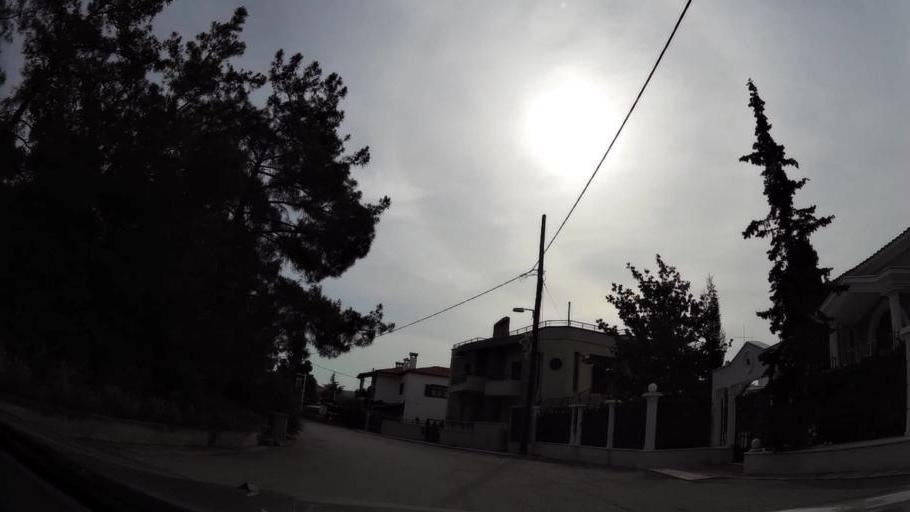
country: GR
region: Central Macedonia
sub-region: Nomos Thessalonikis
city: Panorama
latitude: 40.5864
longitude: 23.0330
